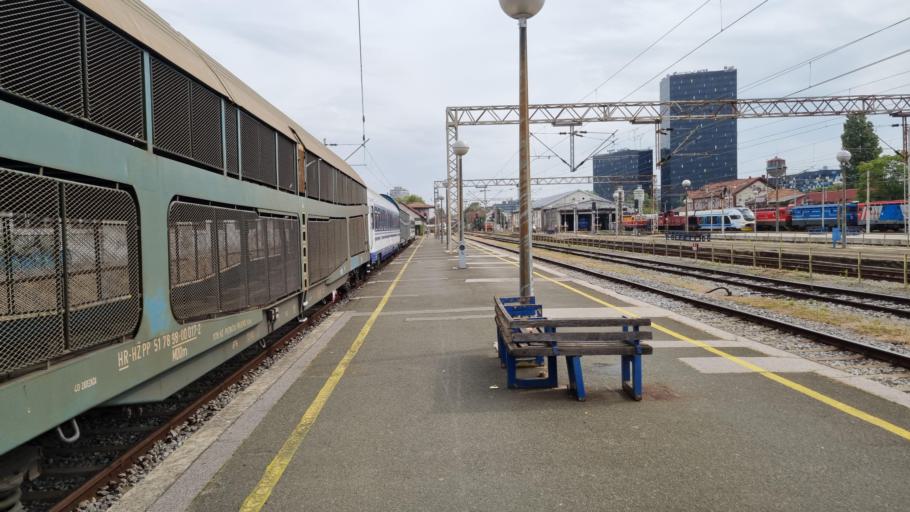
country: HR
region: Grad Zagreb
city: Zagreb - Centar
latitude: 45.8049
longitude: 15.9835
